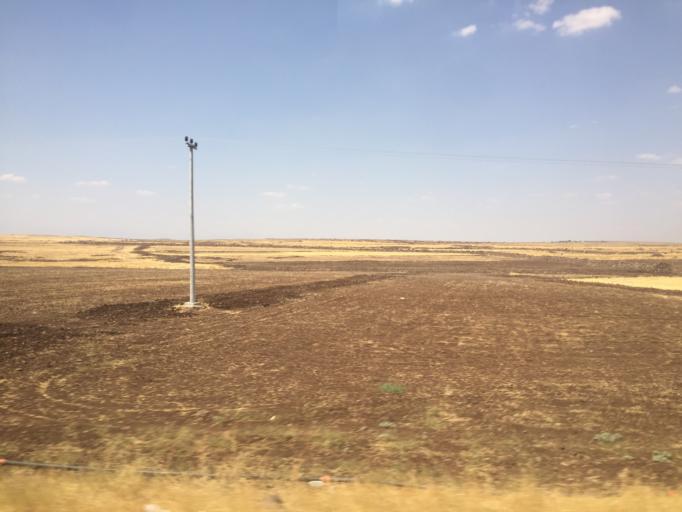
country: TR
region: Sanliurfa
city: Siverek
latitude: 37.7692
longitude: 39.4347
